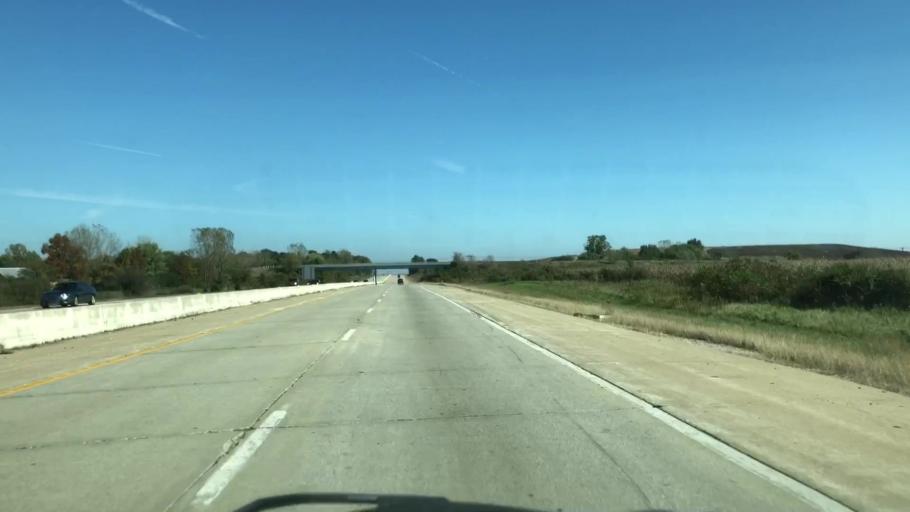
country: US
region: Indiana
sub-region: Elkhart County
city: Elkhart
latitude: 41.6347
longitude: -85.9880
